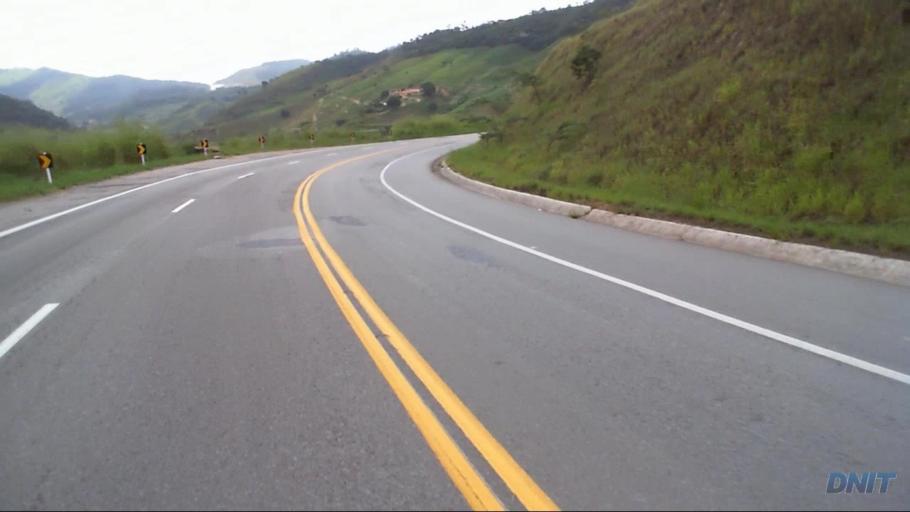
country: BR
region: Minas Gerais
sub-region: Nova Era
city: Nova Era
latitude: -19.6495
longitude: -42.9402
